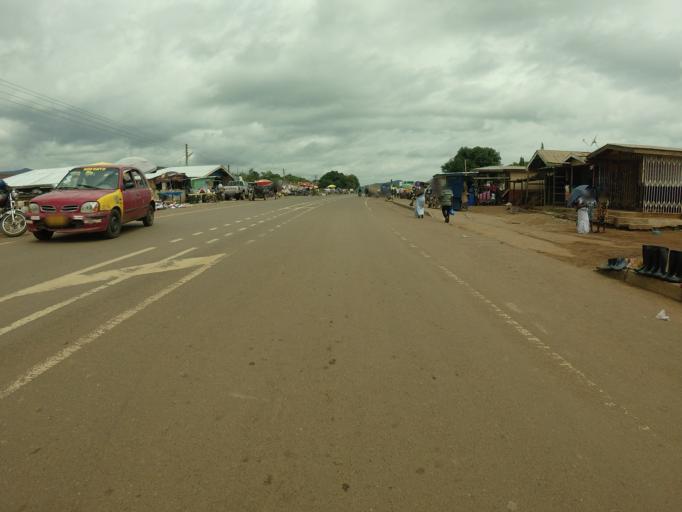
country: TG
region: Centrale
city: Sotouboua
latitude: 8.2612
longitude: 0.5216
